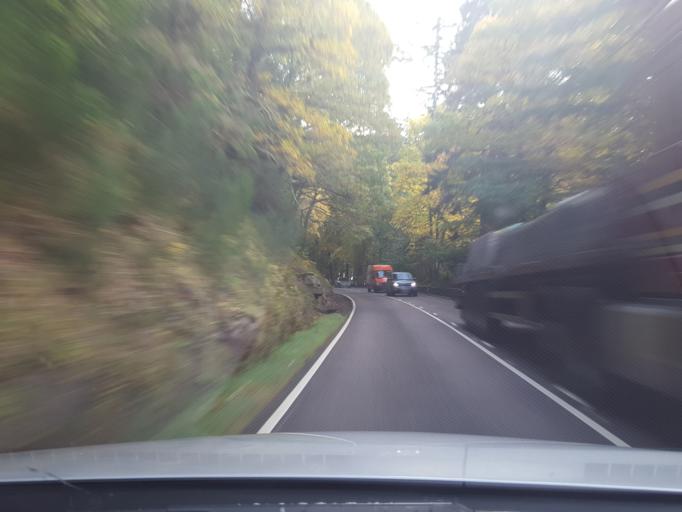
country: GB
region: Scotland
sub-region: Highland
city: Beauly
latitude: 57.2127
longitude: -4.6079
